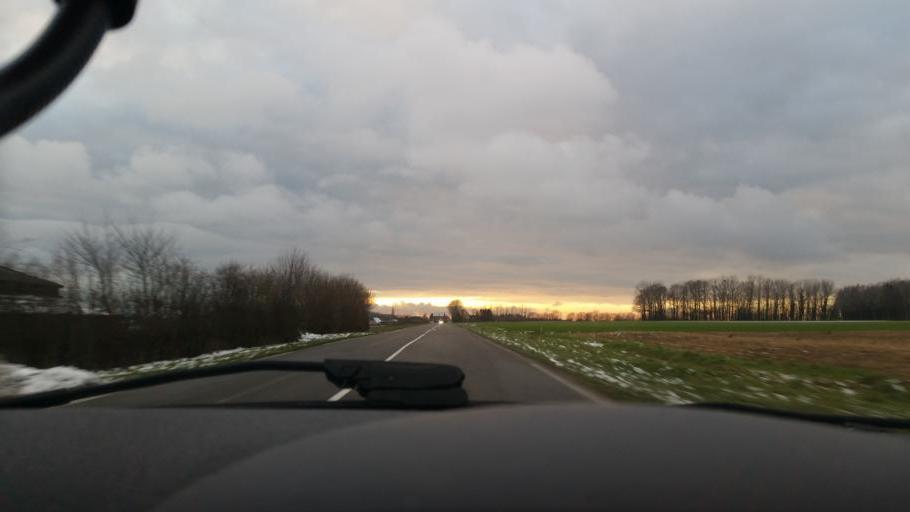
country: FR
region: Nord-Pas-de-Calais
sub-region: Departement du Nord
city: Jeumont
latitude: 50.2507
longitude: 4.1171
